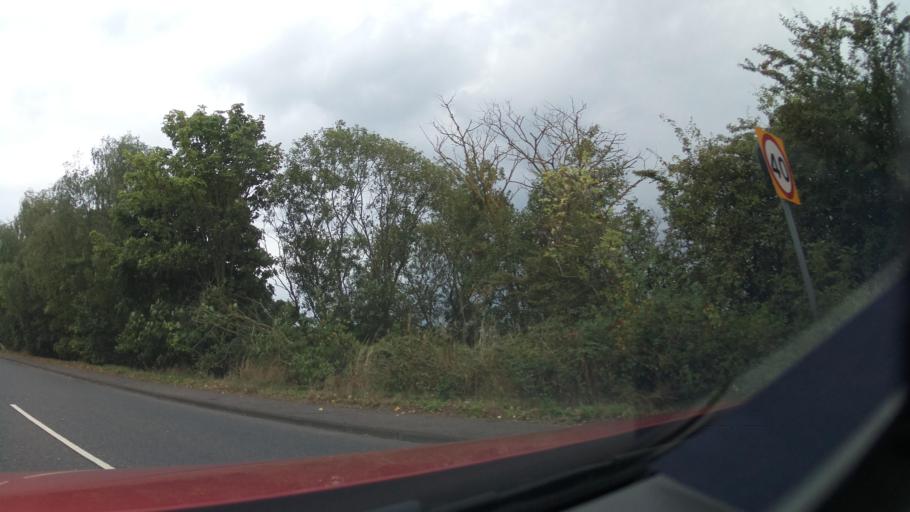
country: GB
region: Scotland
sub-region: East Lothian
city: Musselburgh
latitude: 55.9287
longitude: -3.0393
